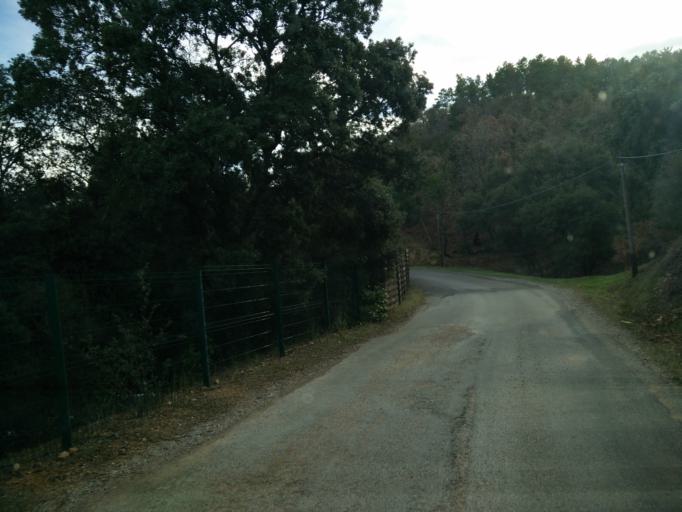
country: FR
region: Provence-Alpes-Cote d'Azur
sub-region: Departement du Var
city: Roquebrune-sur-Argens
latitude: 43.4389
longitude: 6.6347
